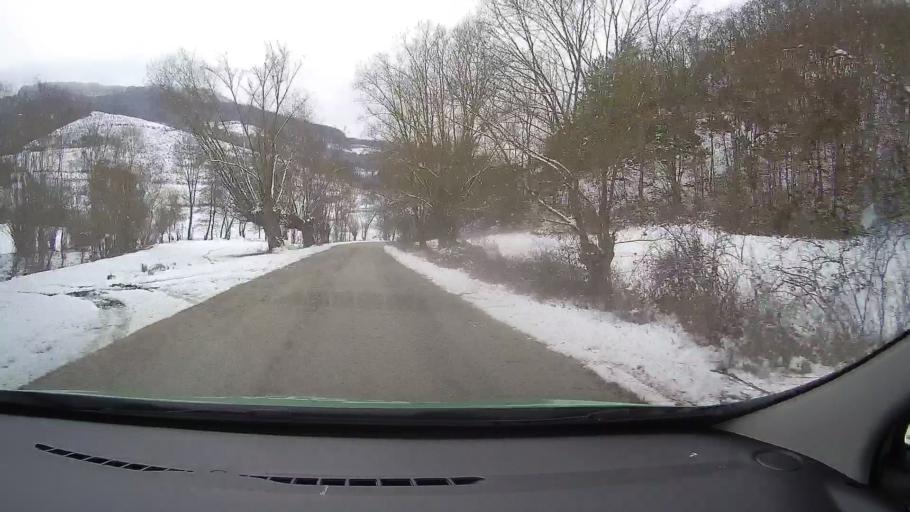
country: RO
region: Hunedoara
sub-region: Comuna Balsa
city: Balsa
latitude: 46.0585
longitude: 23.0923
